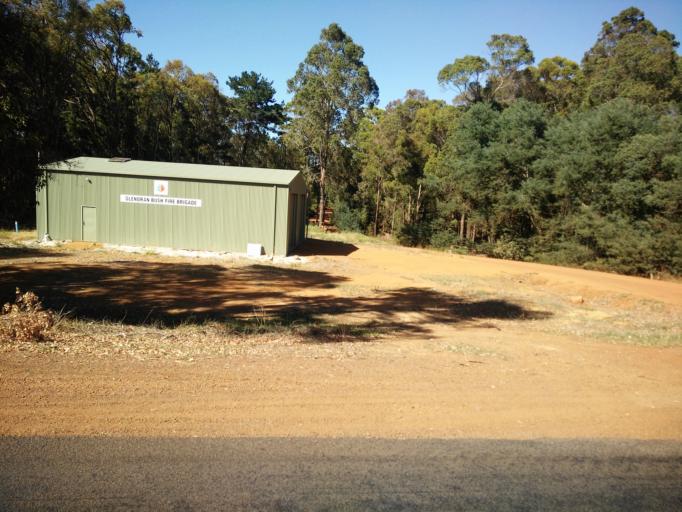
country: AU
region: Western Australia
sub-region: Manjimup
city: Manjimup
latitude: -34.2226
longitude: 115.9891
